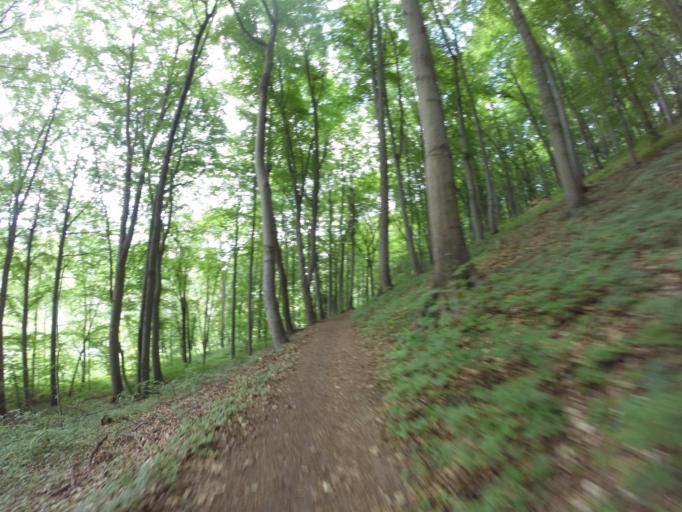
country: DE
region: Thuringia
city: Jena
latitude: 50.9173
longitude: 11.6190
